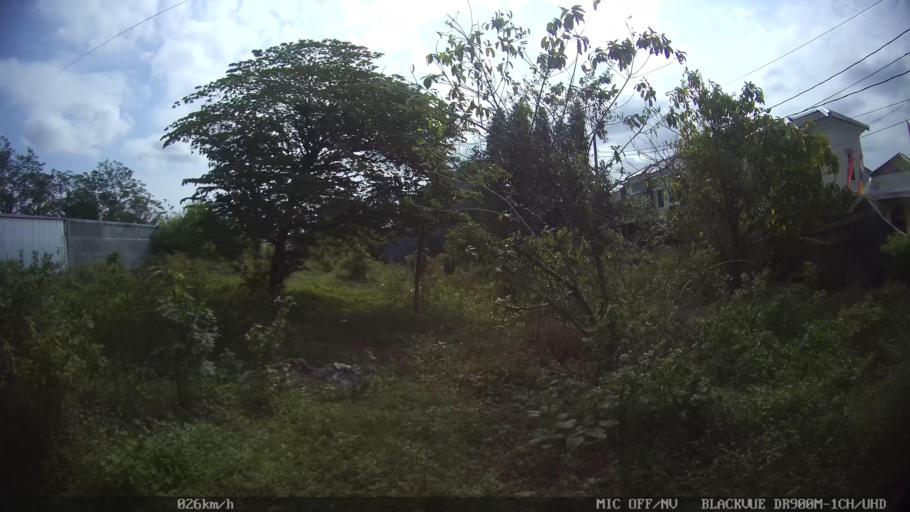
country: ID
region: Daerah Istimewa Yogyakarta
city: Depok
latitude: -7.7611
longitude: 110.4186
